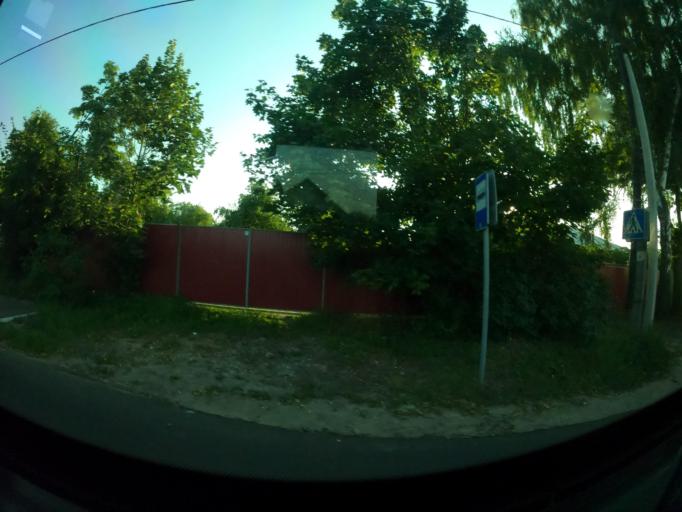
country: RU
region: Moskovskaya
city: Serpukhov
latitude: 54.9330
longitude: 37.3666
